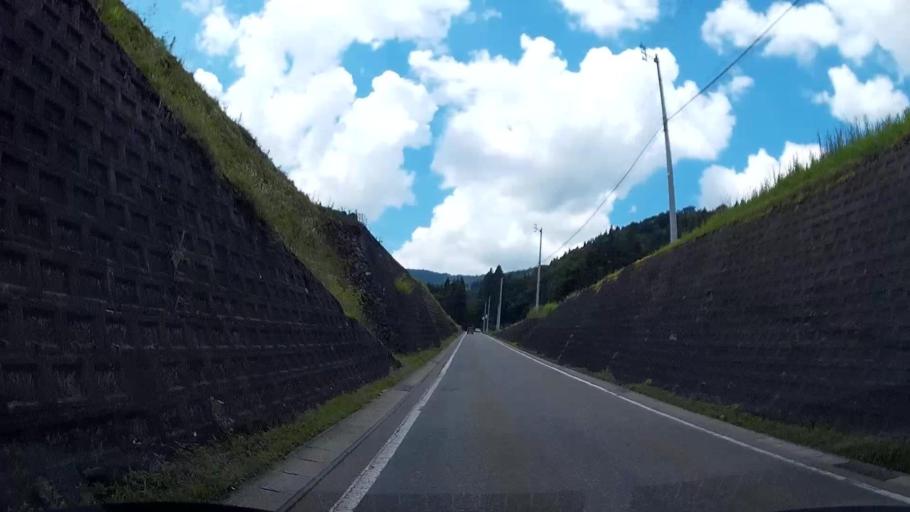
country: JP
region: Niigata
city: Shiozawa
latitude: 37.0185
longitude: 138.8192
